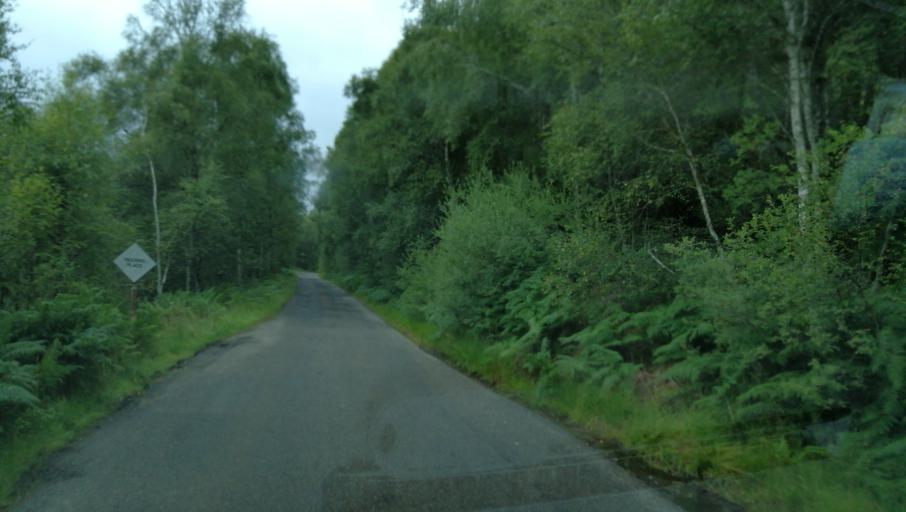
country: GB
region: Scotland
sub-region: Highland
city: Beauly
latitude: 57.3132
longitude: -4.8480
